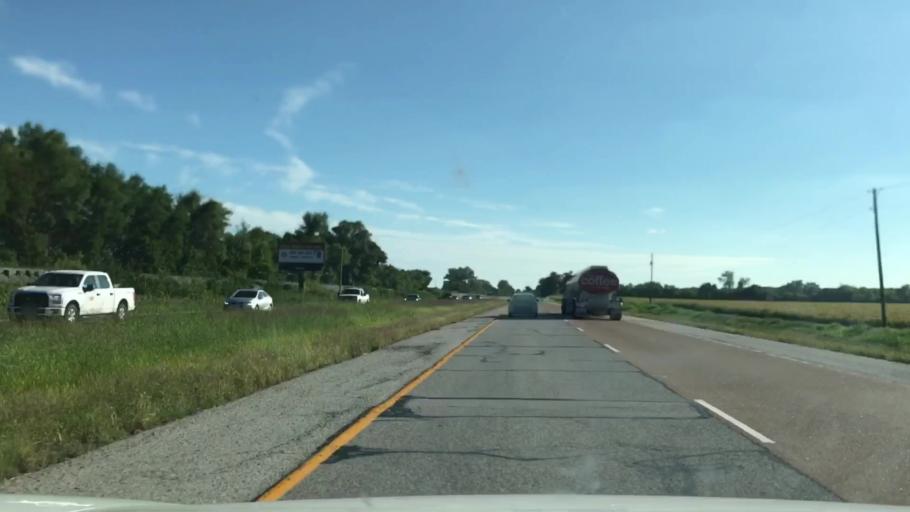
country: US
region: Illinois
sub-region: Madison County
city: Mitchell
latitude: 38.7929
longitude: -90.1036
